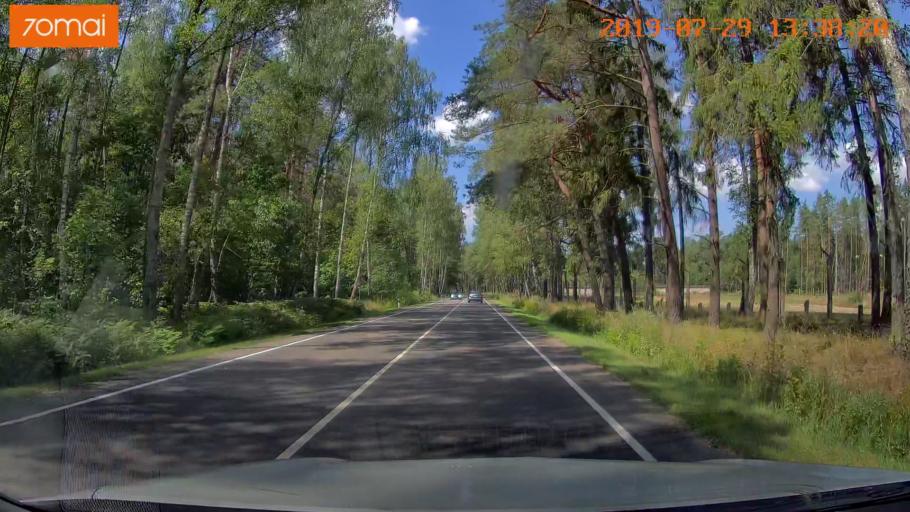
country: RU
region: Kaliningrad
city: Volochayevskoye
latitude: 54.7205
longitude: 20.1722
